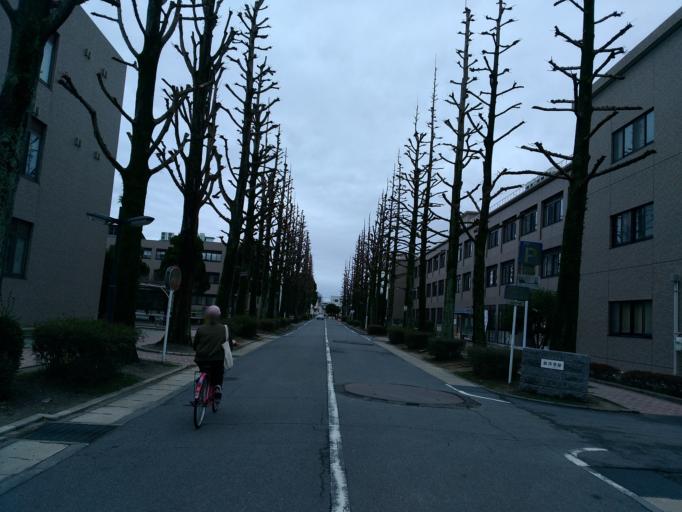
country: JP
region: Saga Prefecture
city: Saga-shi
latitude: 33.2437
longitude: 130.2926
